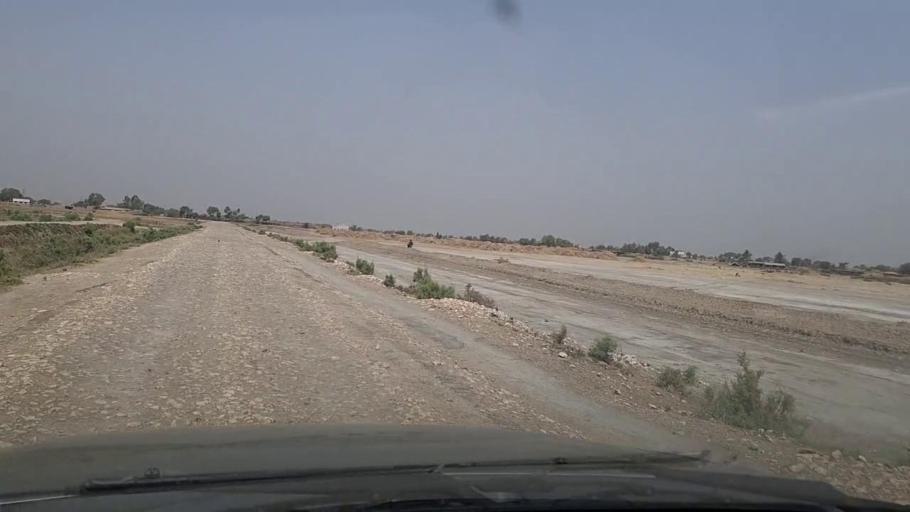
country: PK
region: Balochistan
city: Sohbatpur
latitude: 28.4139
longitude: 68.6917
